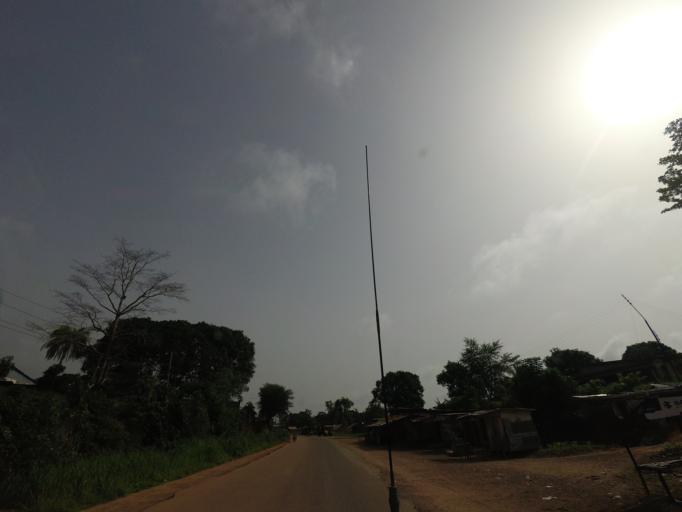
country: SL
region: Southern Province
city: Bo
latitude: 7.9391
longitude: -11.7260
